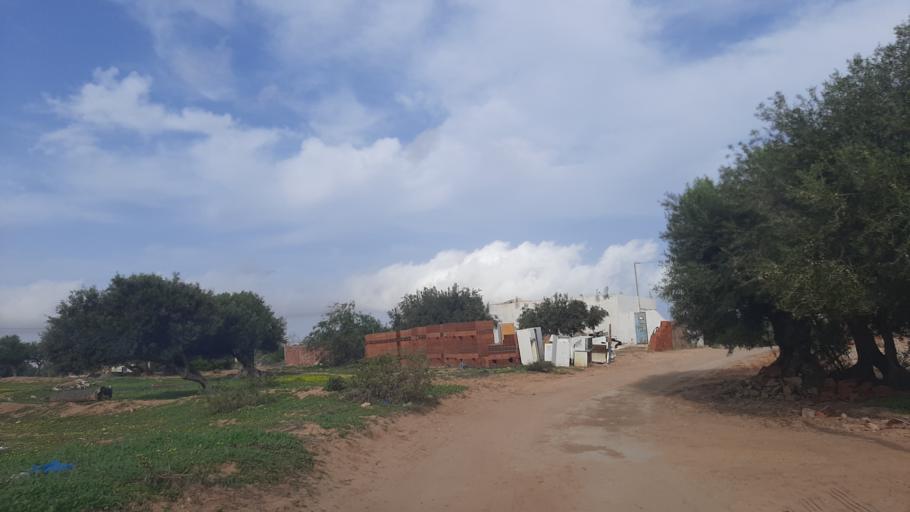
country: TN
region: Madanin
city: Midoun
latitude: 33.8064
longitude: 11.0240
